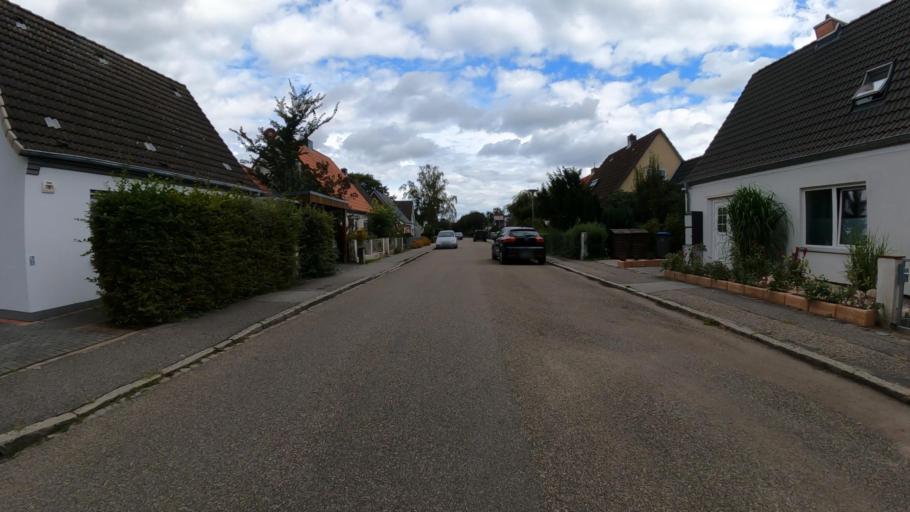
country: DE
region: Schleswig-Holstein
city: Luebeck
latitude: 53.8821
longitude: 10.6834
